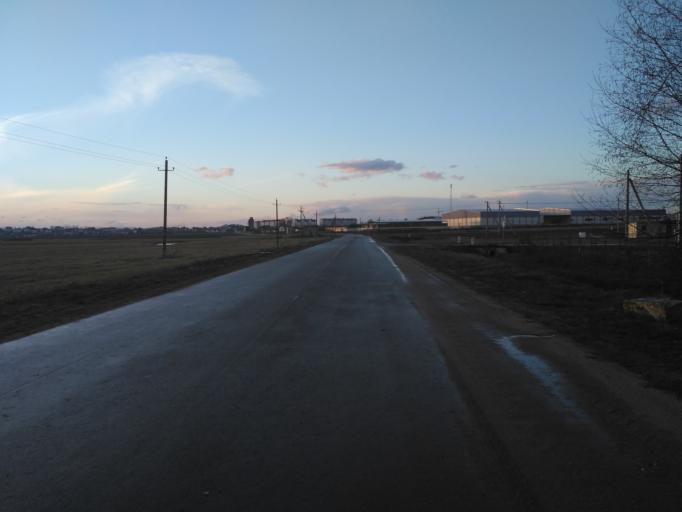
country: BY
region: Minsk
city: Slabada
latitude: 53.9951
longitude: 27.8761
